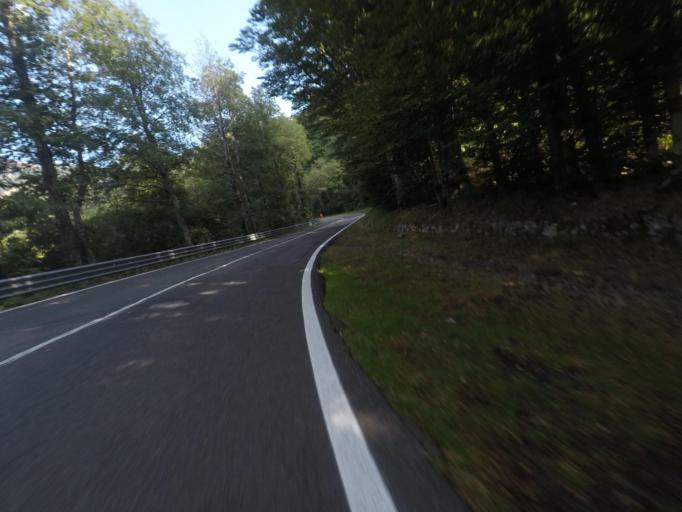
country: IT
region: Tuscany
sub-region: Provincia di Massa-Carrara
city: Comano
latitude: 44.2793
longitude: 10.1863
